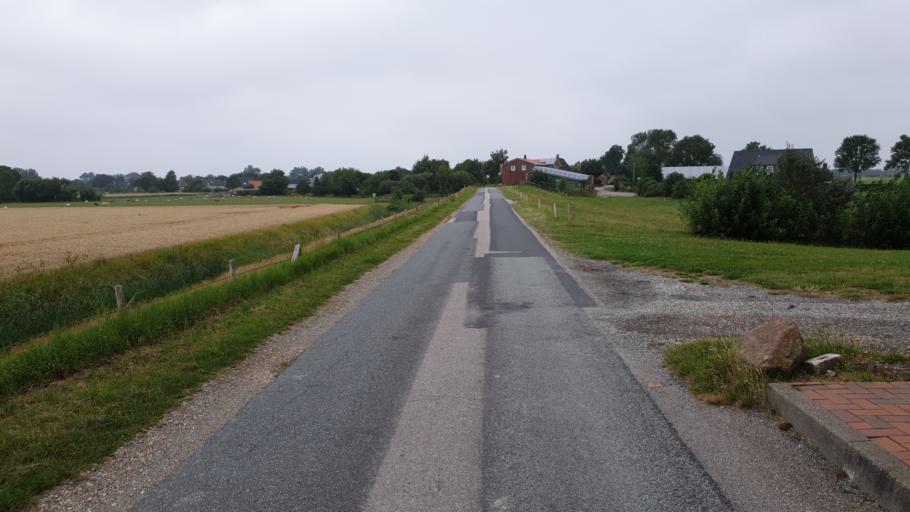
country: DE
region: Schleswig-Holstein
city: Elisabeth-Sophien-Koog
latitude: 54.4864
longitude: 8.8875
